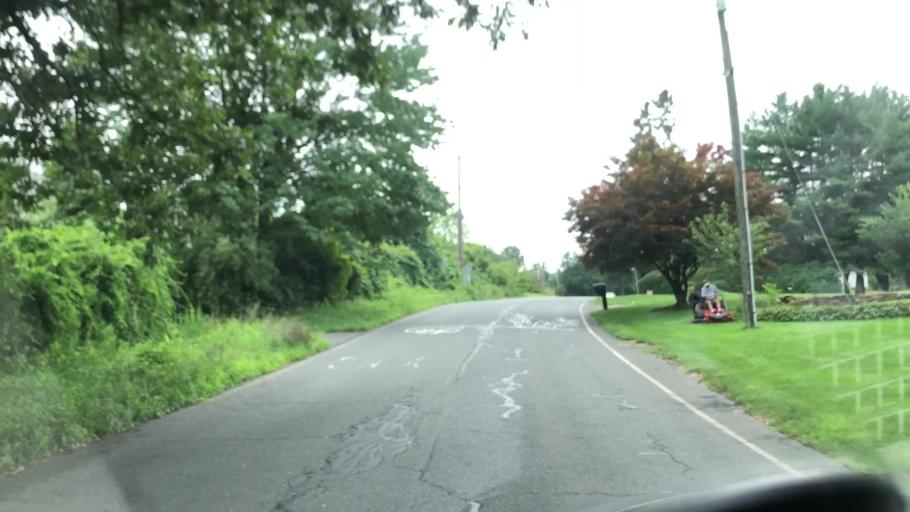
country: US
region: Massachusetts
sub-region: Hampshire County
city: Easthampton
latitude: 42.2508
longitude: -72.6954
